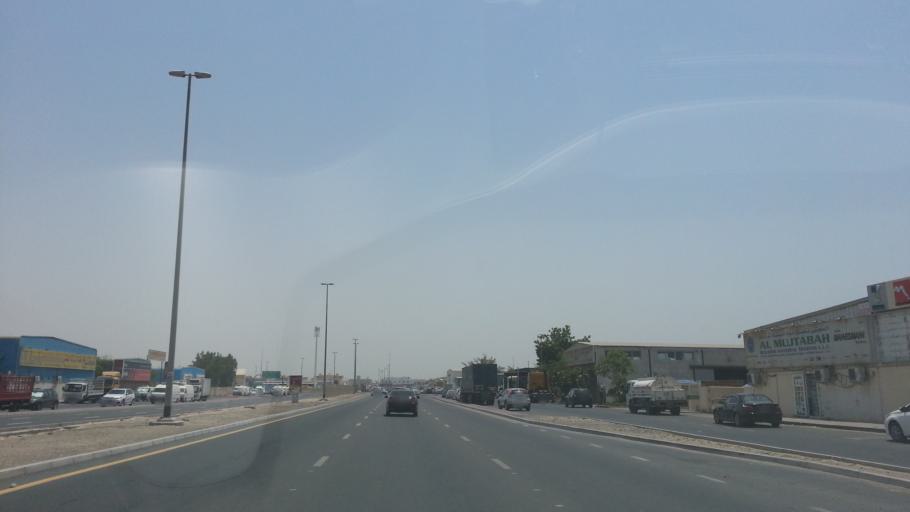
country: AE
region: Dubai
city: Dubai
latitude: 25.1171
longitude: 55.2218
